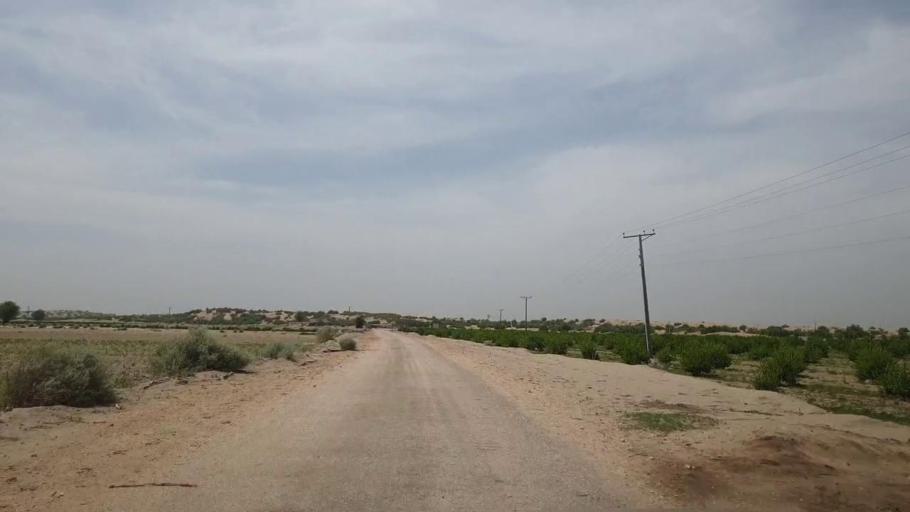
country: PK
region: Sindh
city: Kot Diji
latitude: 27.0827
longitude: 69.0722
